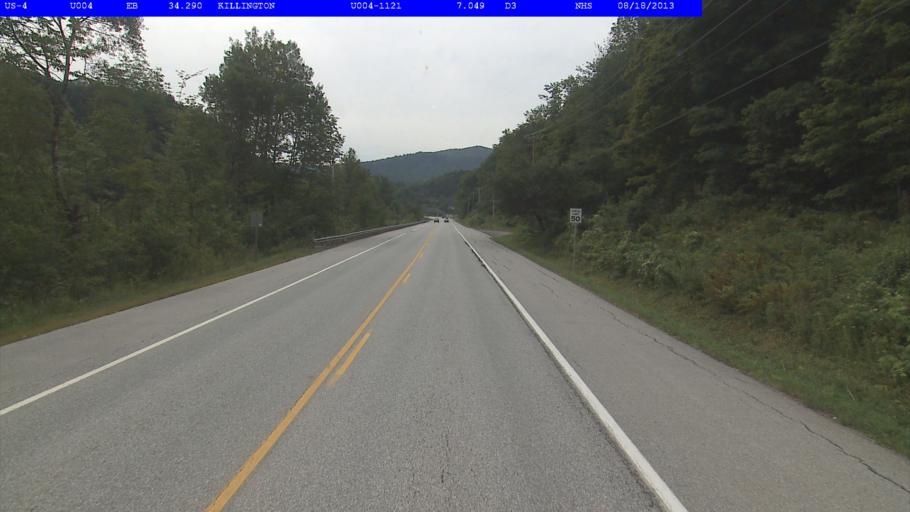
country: US
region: Vermont
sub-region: Rutland County
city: Rutland
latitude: 43.6194
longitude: -72.7592
